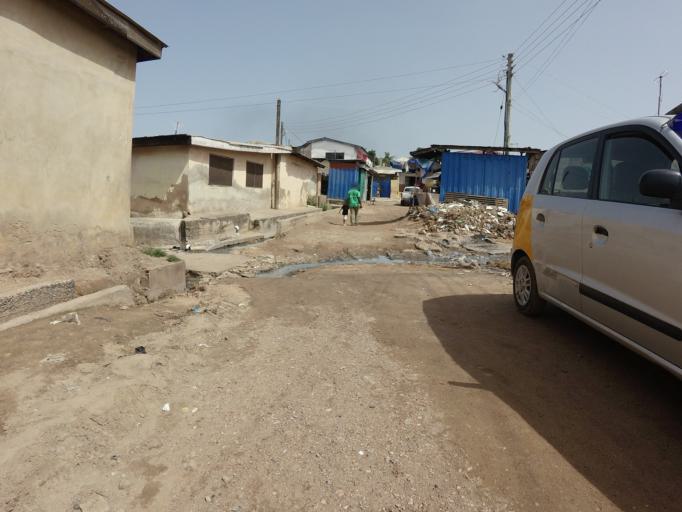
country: GH
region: Greater Accra
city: Dome
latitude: 5.6147
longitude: -0.2375
